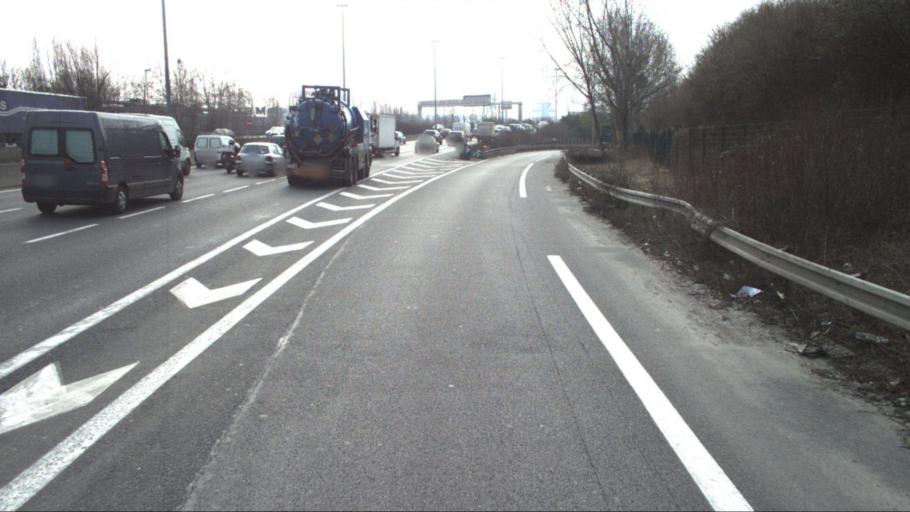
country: FR
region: Ile-de-France
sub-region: Departement des Hauts-de-Seine
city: Villeneuve-la-Garenne
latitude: 48.9368
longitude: 2.3178
